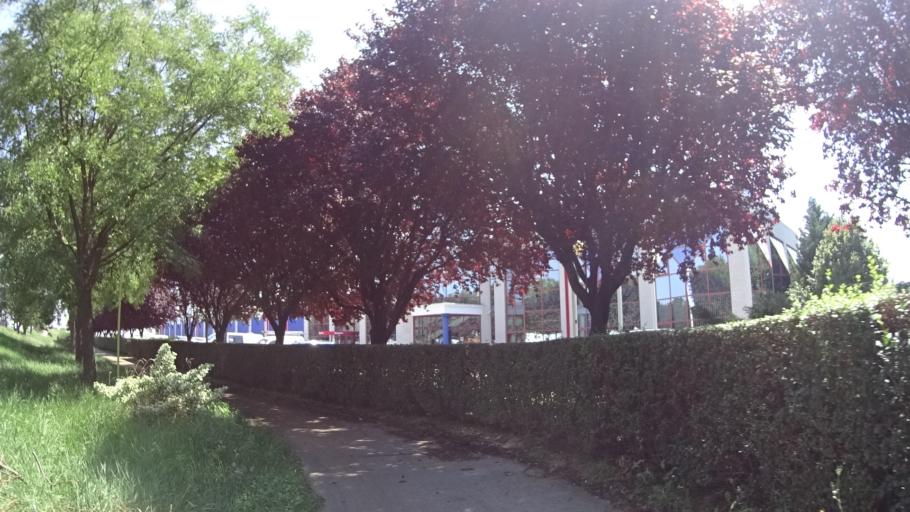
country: HU
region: Fejer
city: Szekesfehervar
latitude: 47.1960
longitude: 18.4715
